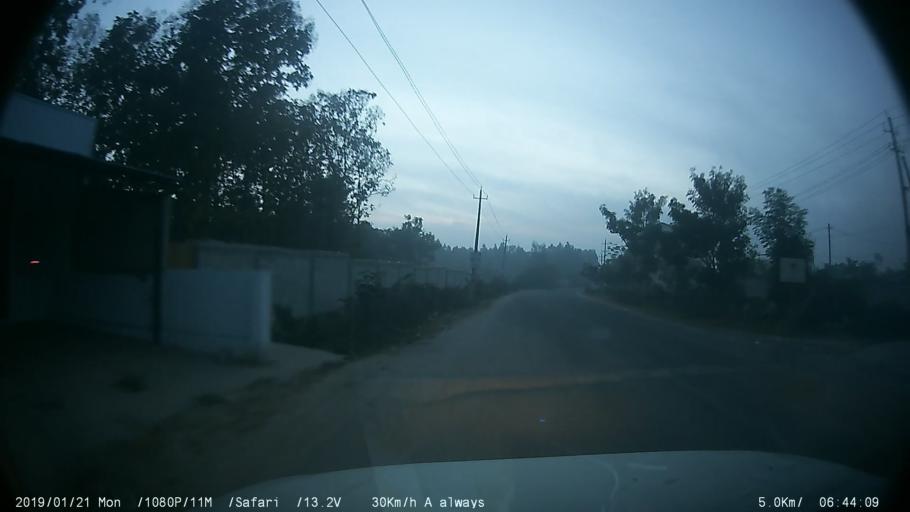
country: IN
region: Karnataka
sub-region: Bangalore Urban
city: Anekal
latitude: 12.8201
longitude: 77.6250
